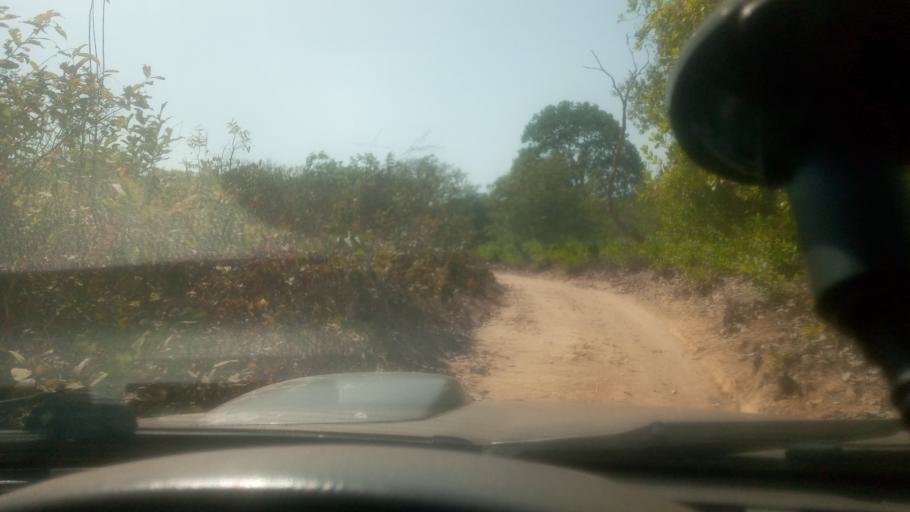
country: GW
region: Oio
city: Farim
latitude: 12.4534
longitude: -15.4179
